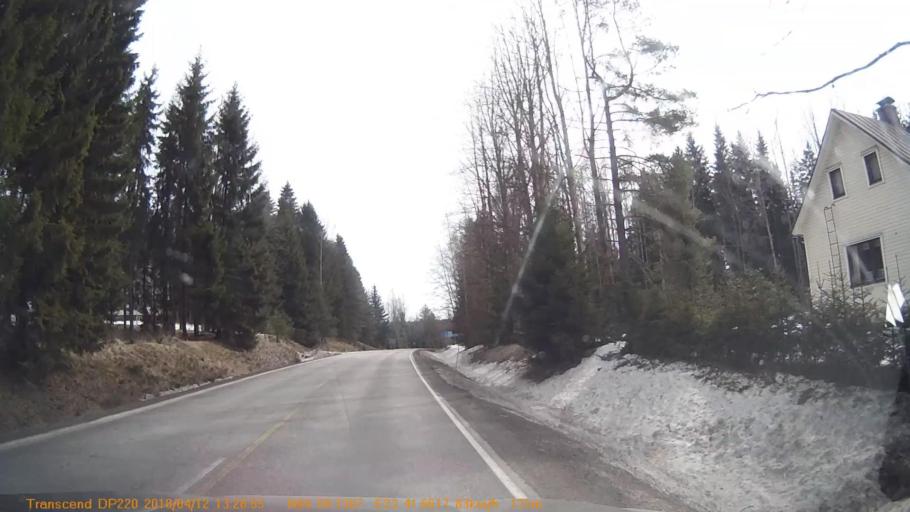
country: FI
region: Pirkanmaa
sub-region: Etelae-Pirkanmaa
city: Kylmaekoski
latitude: 60.9786
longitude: 23.6945
